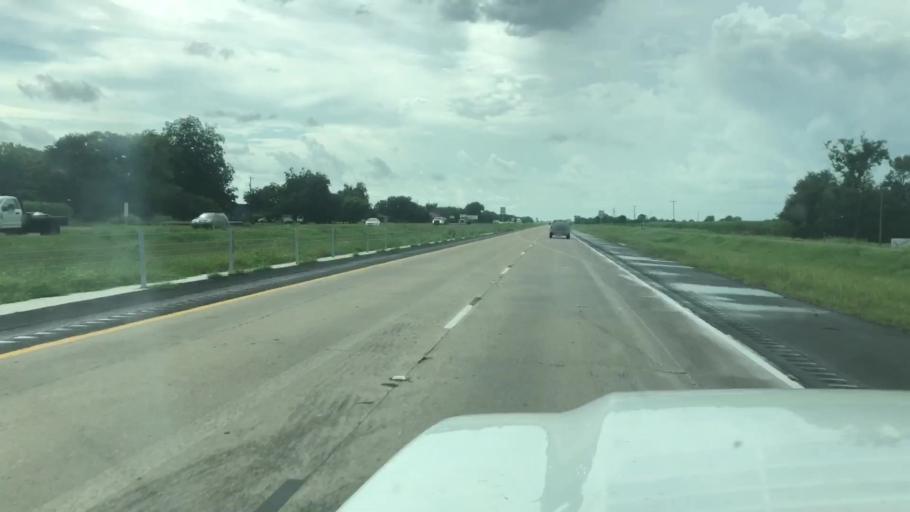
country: US
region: Louisiana
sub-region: Iberia Parish
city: Jeanerette
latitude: 29.8708
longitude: -91.6419
